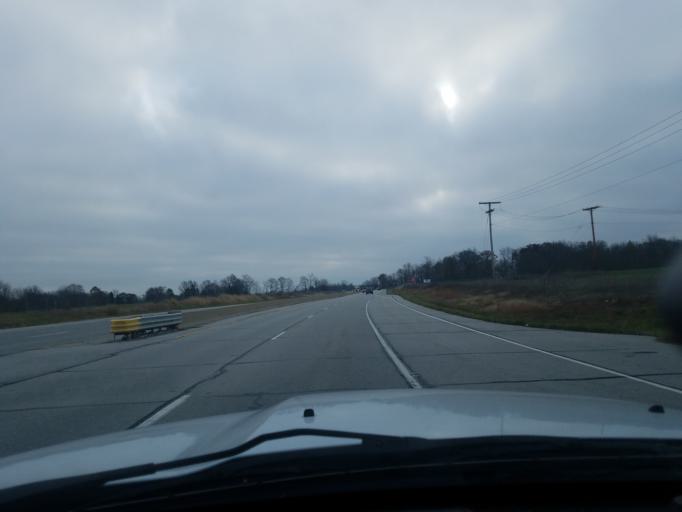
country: US
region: Indiana
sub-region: Delaware County
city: Yorktown
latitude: 40.2184
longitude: -85.5530
